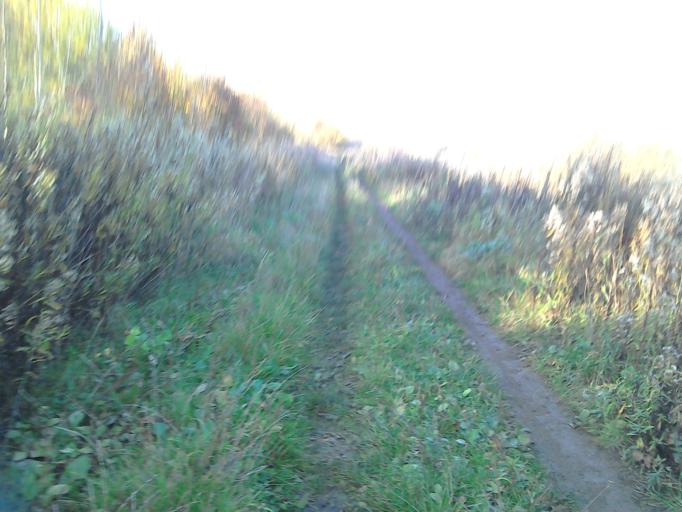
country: GB
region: England
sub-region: Oxfordshire
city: Radley
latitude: 51.6975
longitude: -1.2297
